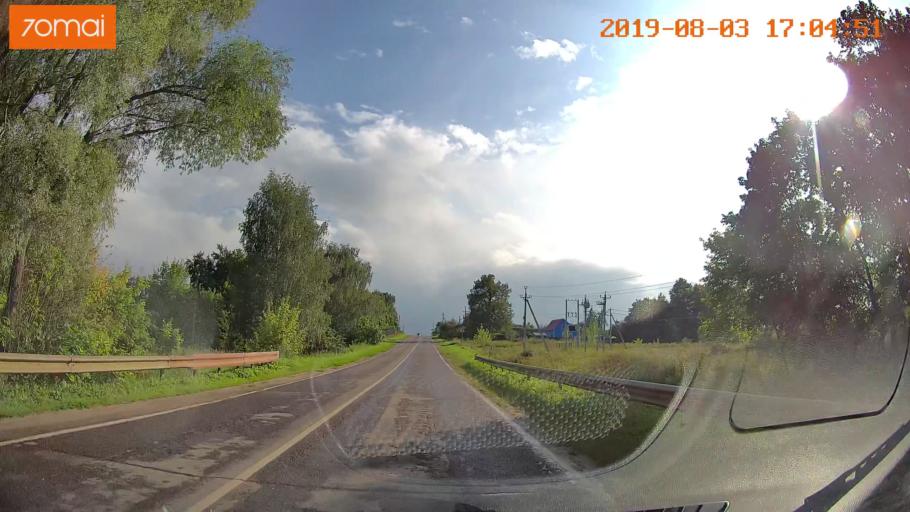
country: RU
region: Moskovskaya
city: Troitskoye
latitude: 55.3255
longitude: 38.5546
